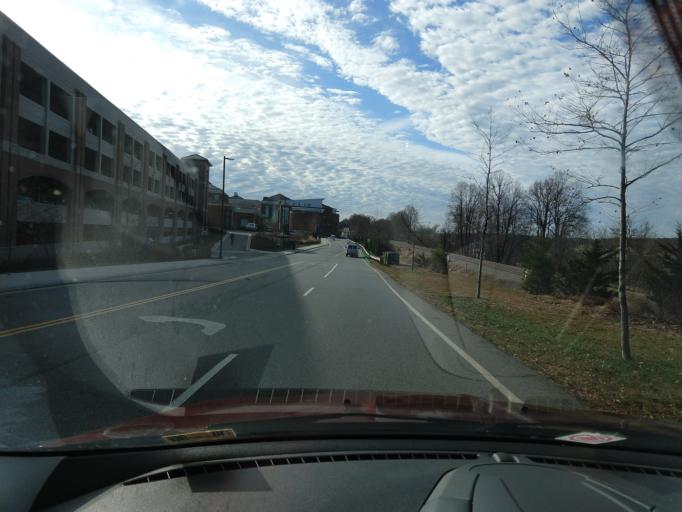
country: US
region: Virginia
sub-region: City of Lynchburg
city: West Lynchburg
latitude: 37.3540
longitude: -79.1815
